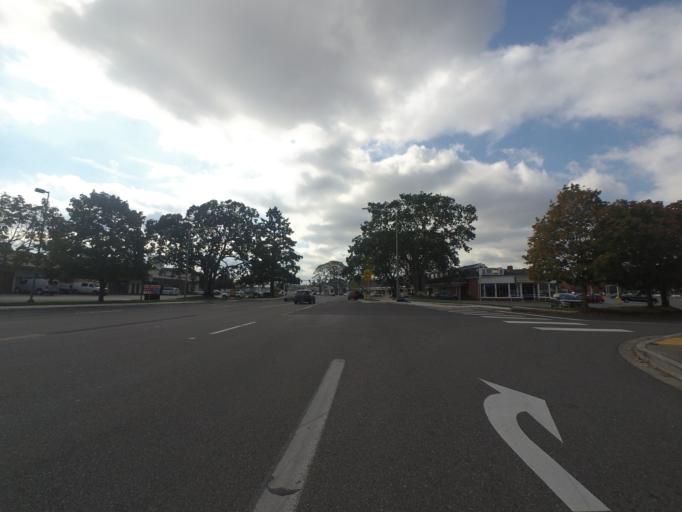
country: US
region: Washington
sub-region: Pierce County
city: Lakewood
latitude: 47.1714
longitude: -122.5192
